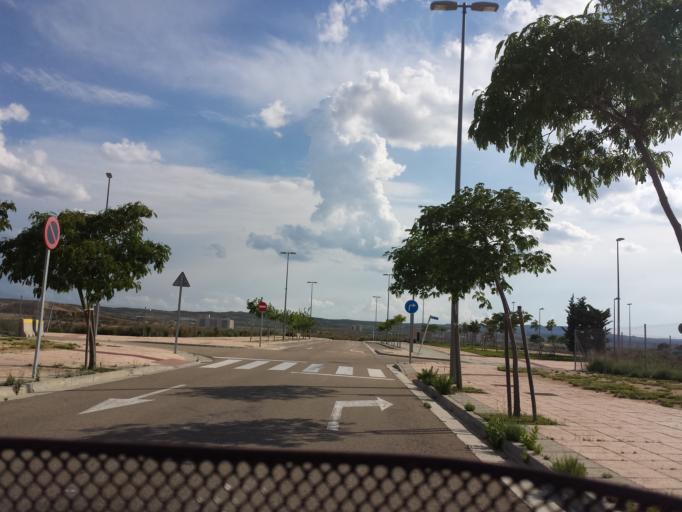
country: ES
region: Aragon
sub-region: Provincia de Zaragoza
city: Montecanal
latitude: 41.6369
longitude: -0.9526
